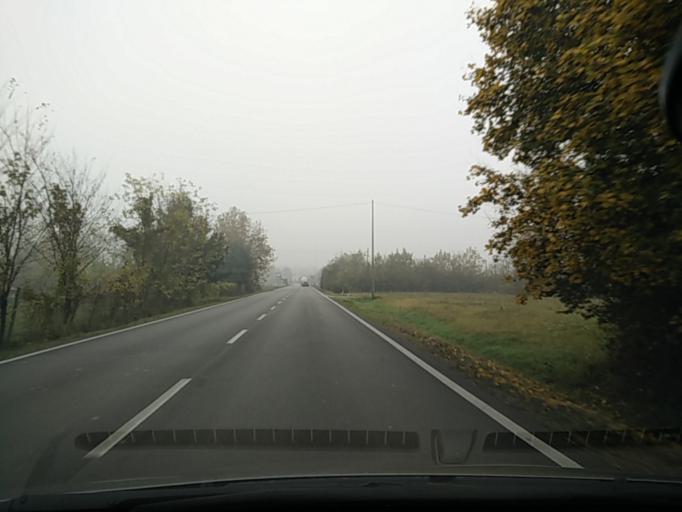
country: IT
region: Veneto
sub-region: Provincia di Venezia
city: Salzano
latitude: 45.5143
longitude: 12.1090
